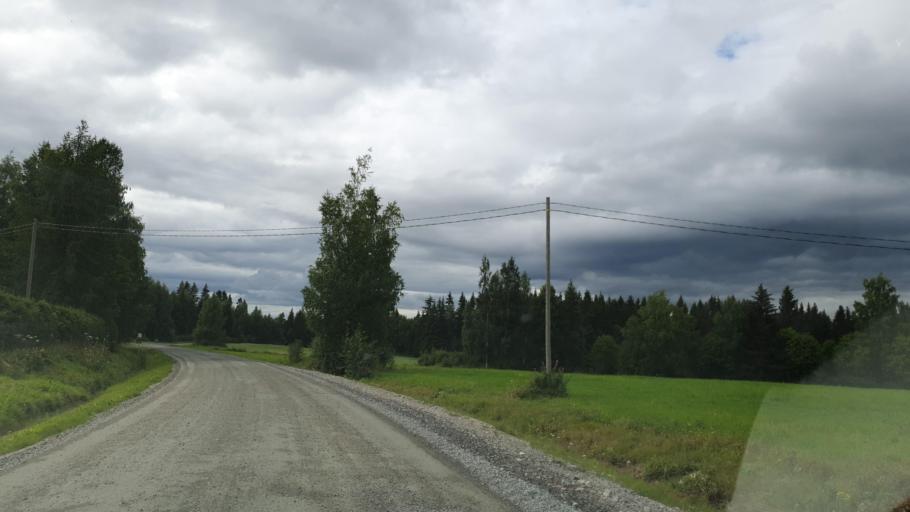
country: FI
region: Northern Savo
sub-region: Ylae-Savo
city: Iisalmi
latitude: 63.5367
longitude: 27.0817
